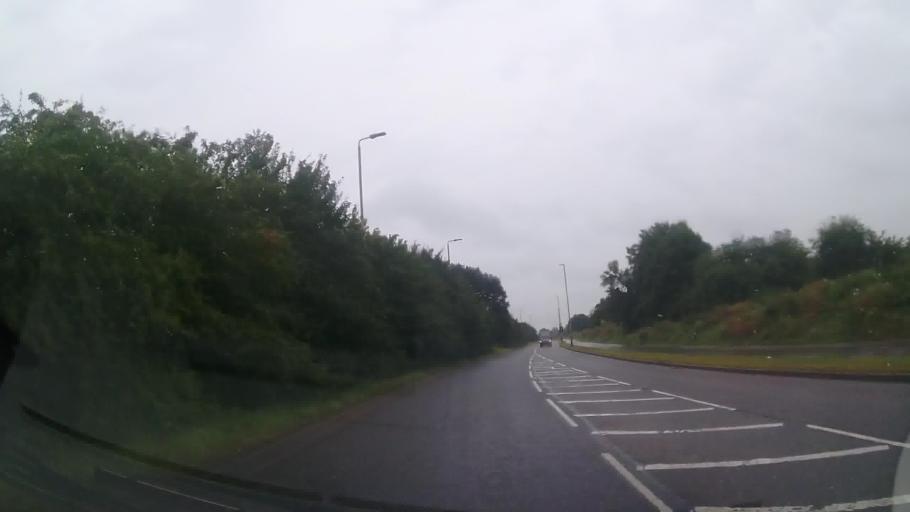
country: GB
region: England
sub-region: Leicestershire
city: Mountsorrel
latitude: 52.6793
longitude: -1.1468
